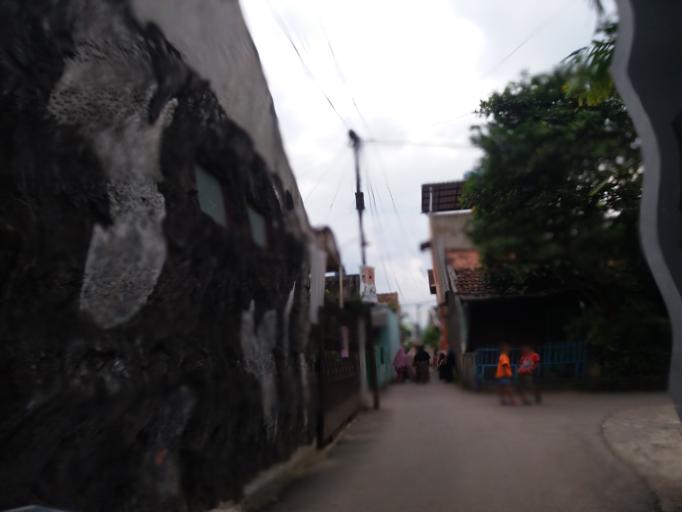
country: ID
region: West Java
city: Bandung
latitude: -6.9223
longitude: 107.6525
